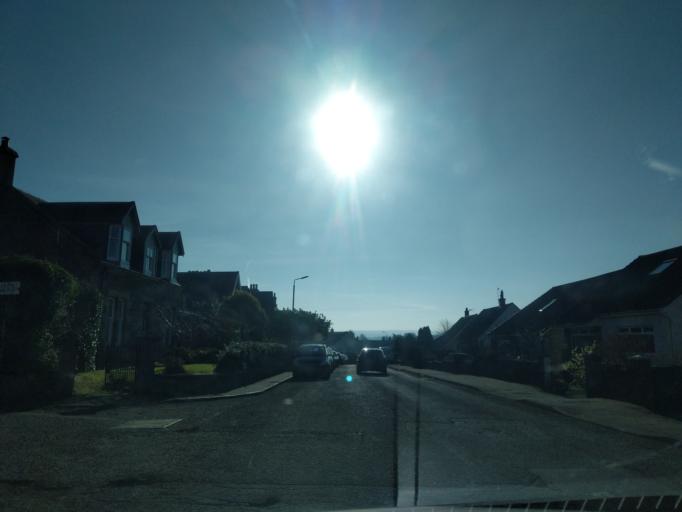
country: GB
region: Scotland
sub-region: South Lanarkshire
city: Lanark
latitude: 55.6708
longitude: -3.7757
